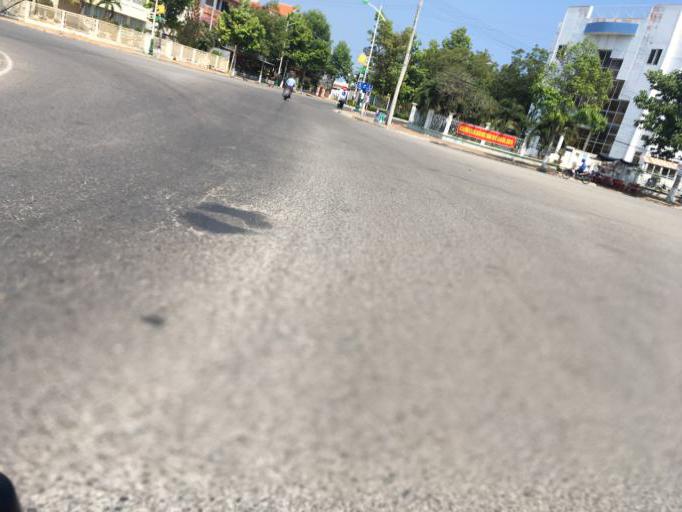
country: VN
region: Ninh Thuan
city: Phan Rang-Thap Cham
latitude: 11.5649
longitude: 109.0006
